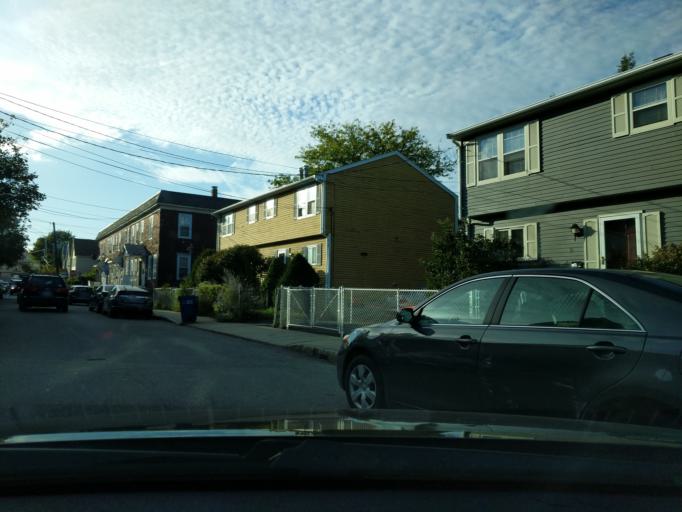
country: US
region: Massachusetts
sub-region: Middlesex County
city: Cambridge
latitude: 42.3773
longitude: -71.1001
